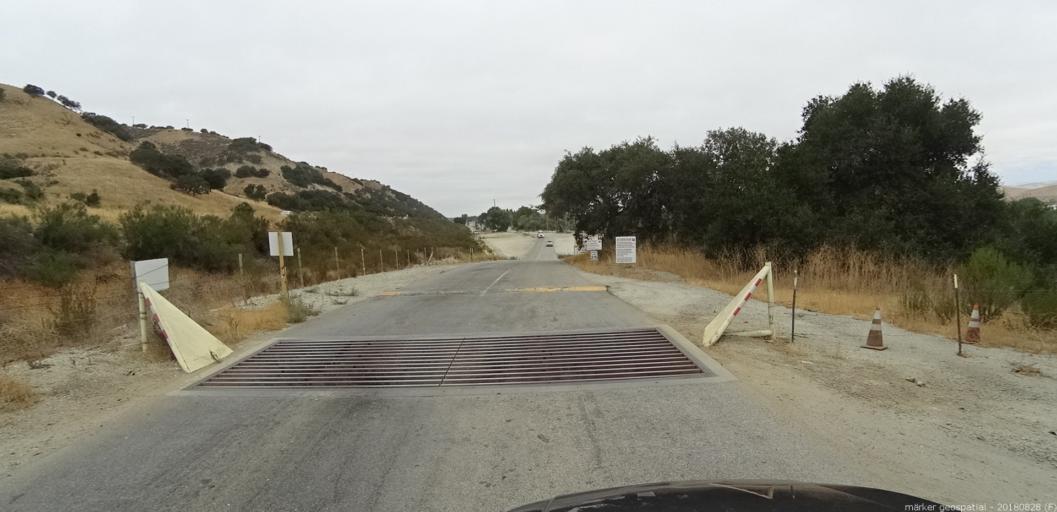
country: US
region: California
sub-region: San Luis Obispo County
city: Lake Nacimiento
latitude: 35.9481
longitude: -120.8757
